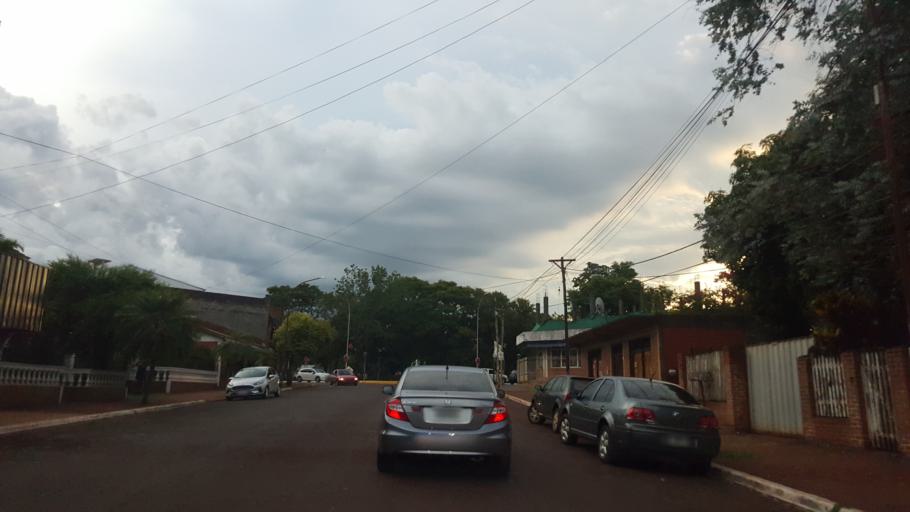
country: AR
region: Misiones
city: Jardin America
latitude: -27.0420
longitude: -55.2258
